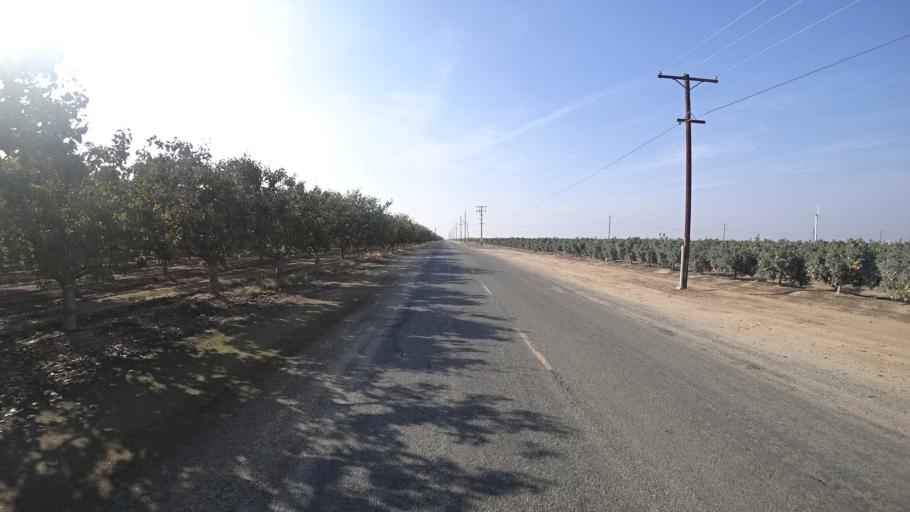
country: US
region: California
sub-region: Tulare County
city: Richgrove
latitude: 35.7908
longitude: -119.0871
